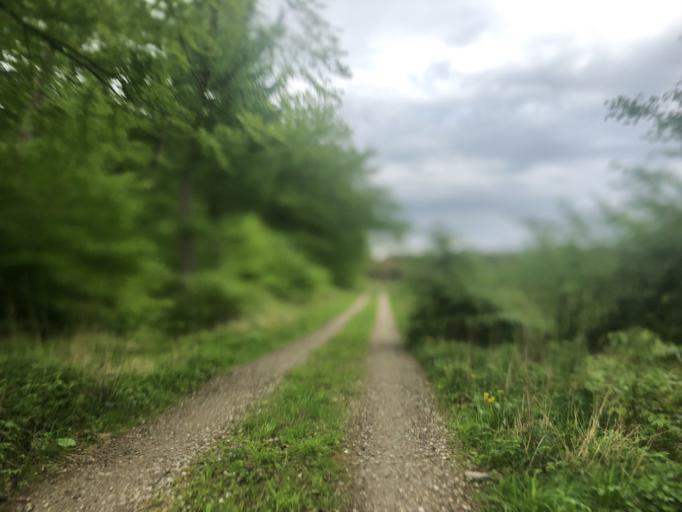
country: DK
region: Zealand
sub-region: Koge Kommune
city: Ejby
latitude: 55.4408
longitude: 12.0904
